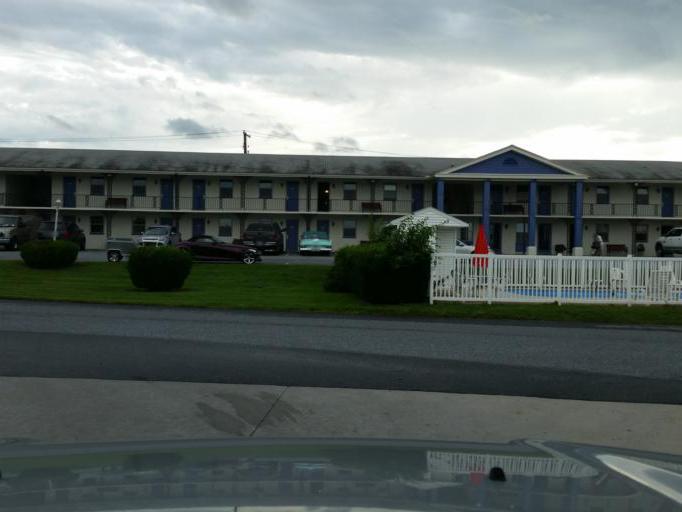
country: US
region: Pennsylvania
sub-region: Cumberland County
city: Mechanicsburg
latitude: 40.1944
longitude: -76.9782
